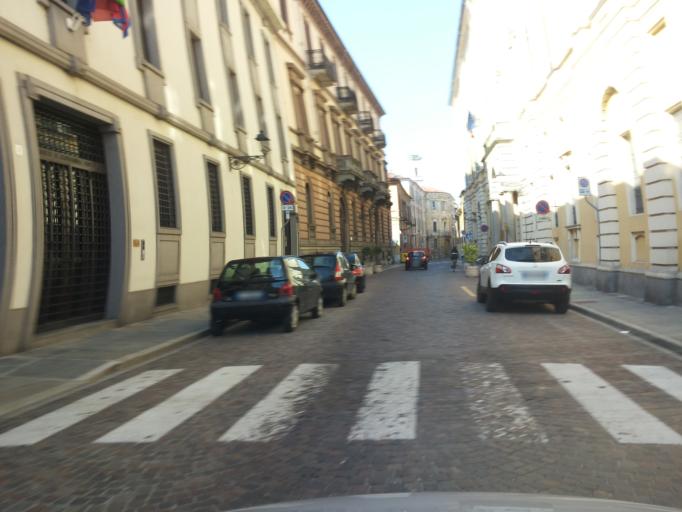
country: IT
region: Piedmont
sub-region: Provincia di Vercelli
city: Vercelli
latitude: 45.3228
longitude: 8.4238
